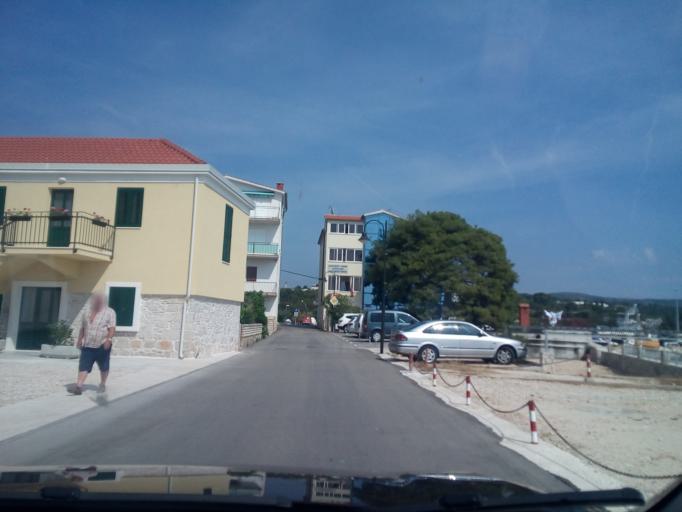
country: HR
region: Sibensko-Kniniska
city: Primosten
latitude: 43.5855
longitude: 15.9278
